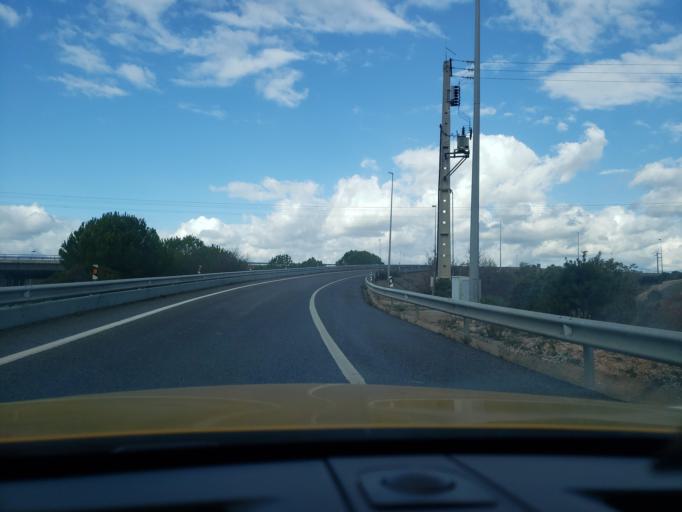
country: PT
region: Faro
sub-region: Portimao
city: Portimao
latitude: 37.1748
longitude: -8.5673
